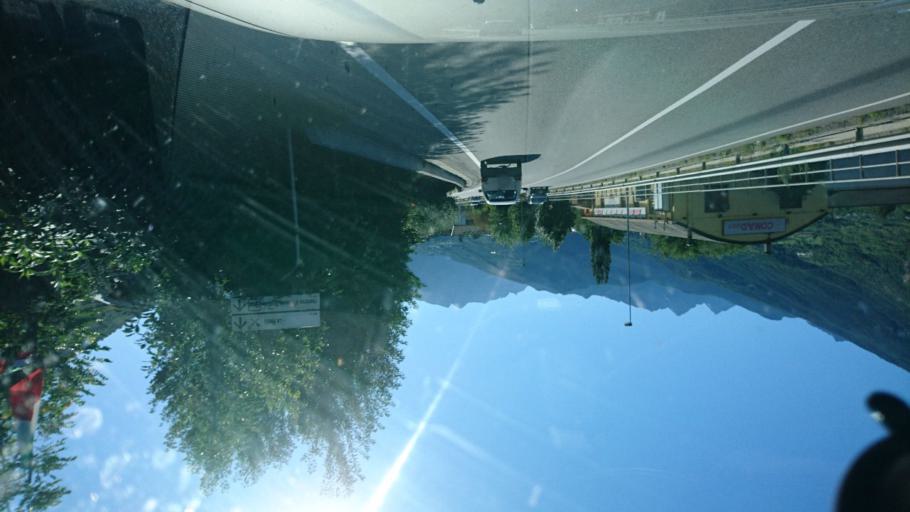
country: IT
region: Aosta Valley
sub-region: Valle d'Aosta
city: Jovencan
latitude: 45.7222
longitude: 7.2684
